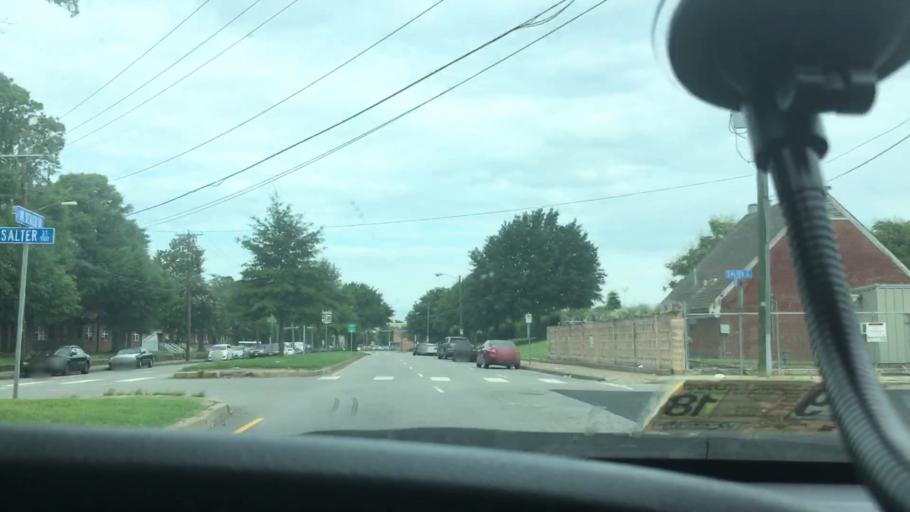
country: US
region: Virginia
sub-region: City of Norfolk
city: Norfolk
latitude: 36.8578
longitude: -76.2844
